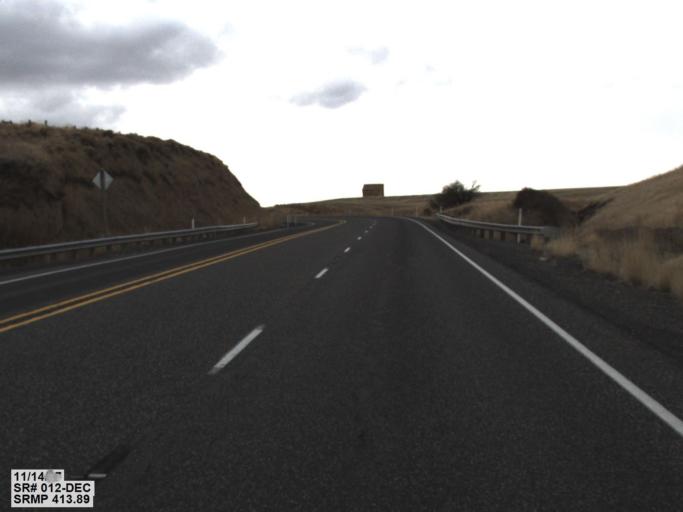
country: US
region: Washington
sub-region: Garfield County
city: Pomeroy
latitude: 46.4383
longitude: -117.4138
